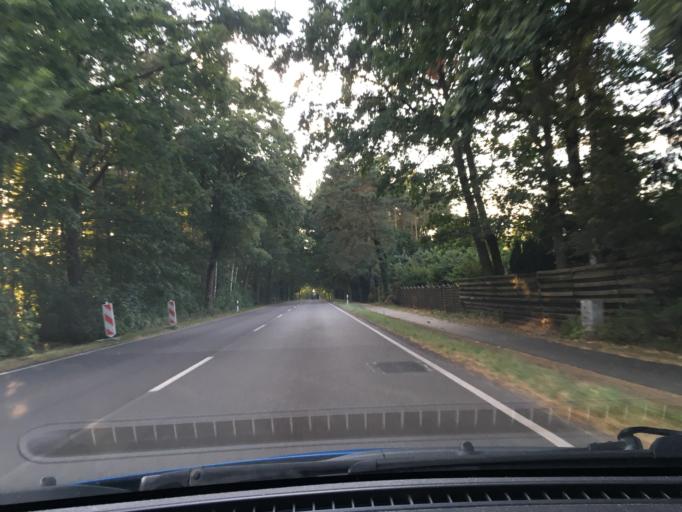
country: DE
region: Lower Saxony
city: Celle
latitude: 52.6581
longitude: 10.0549
